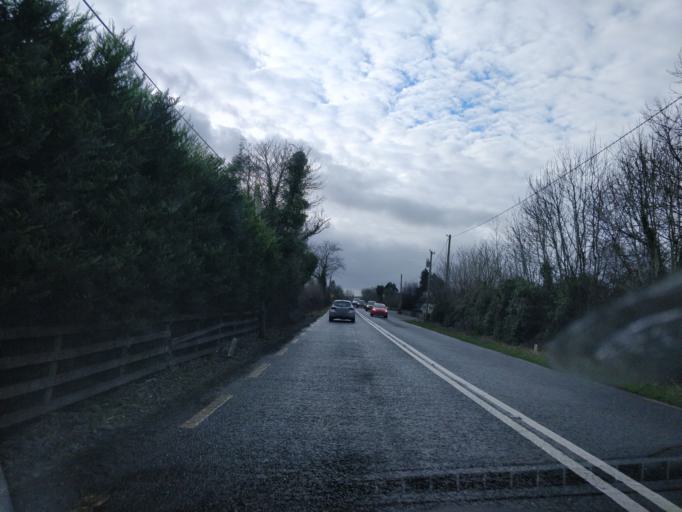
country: IE
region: Connaught
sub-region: Roscommon
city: Roscommon
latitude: 53.7665
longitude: -8.1727
